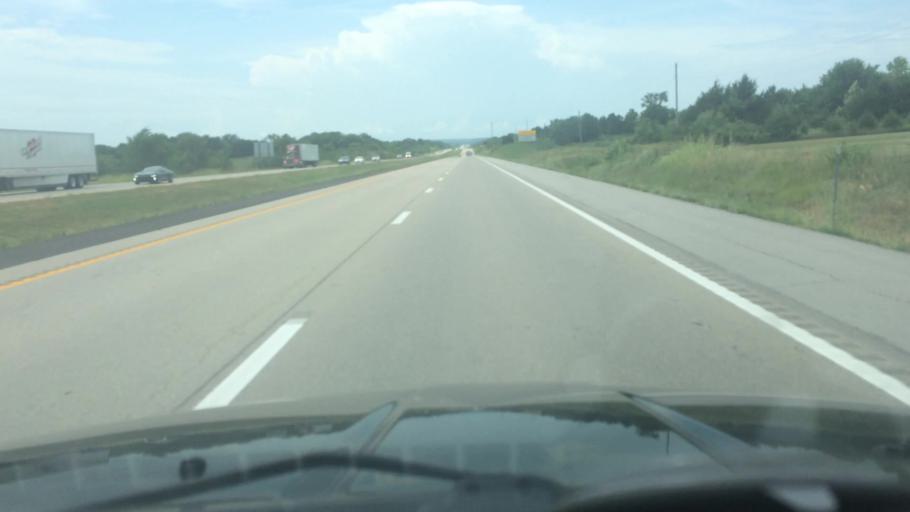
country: US
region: Missouri
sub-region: Polk County
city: Humansville
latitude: 37.7664
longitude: -93.5613
